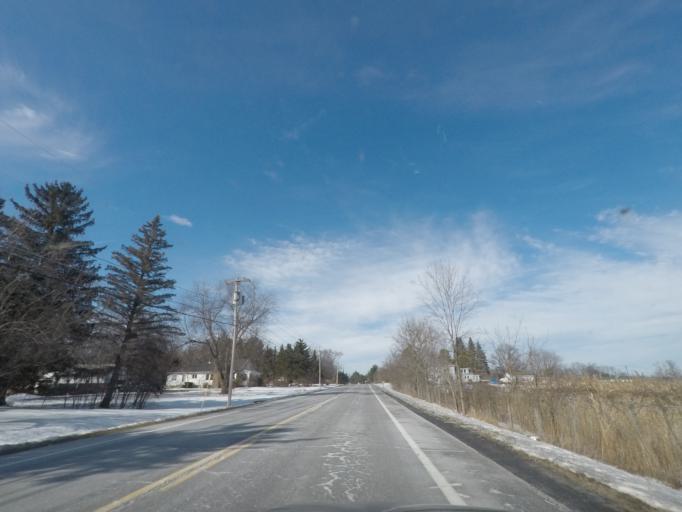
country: US
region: New York
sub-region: Albany County
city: Voorheesville
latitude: 42.6908
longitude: -73.9654
